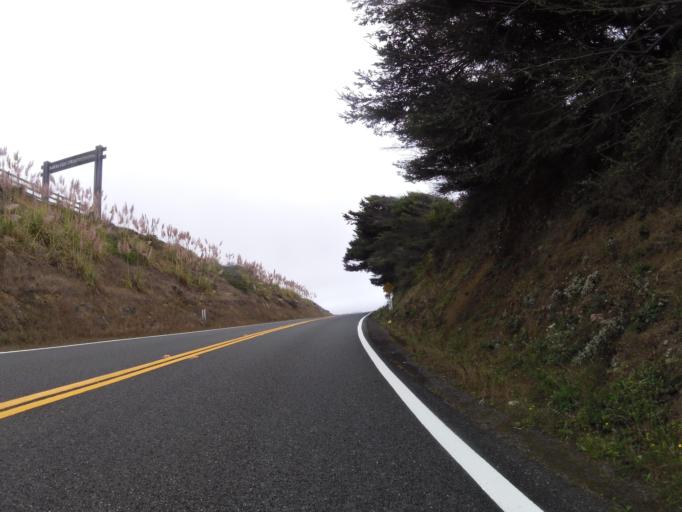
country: US
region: California
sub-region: Sonoma County
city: Monte Rio
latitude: 38.4652
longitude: -123.1518
